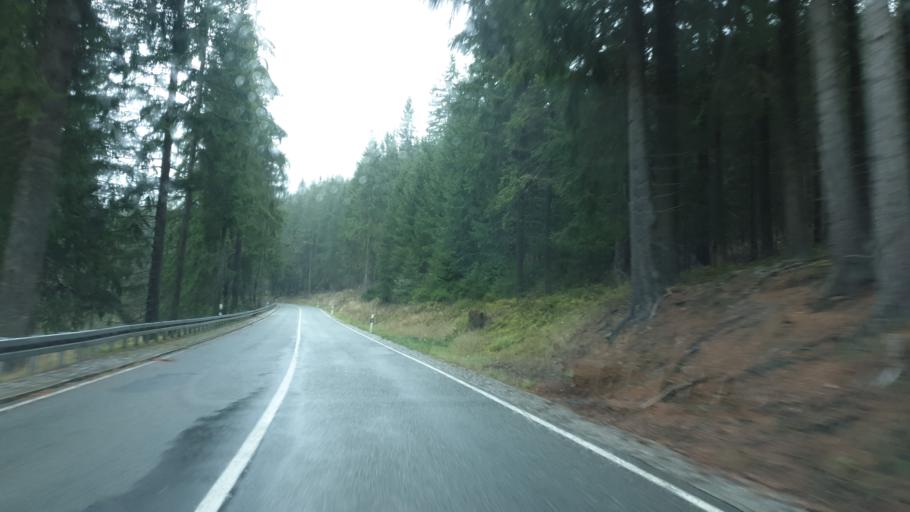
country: DE
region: Saxony
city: Muldenhammer
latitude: 50.4672
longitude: 12.5046
